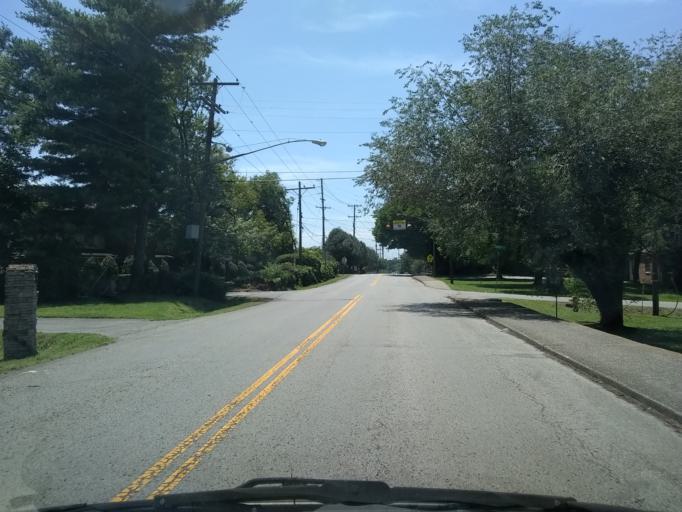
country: US
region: Tennessee
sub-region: Davidson County
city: Oak Hill
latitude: 36.1272
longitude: -86.7046
